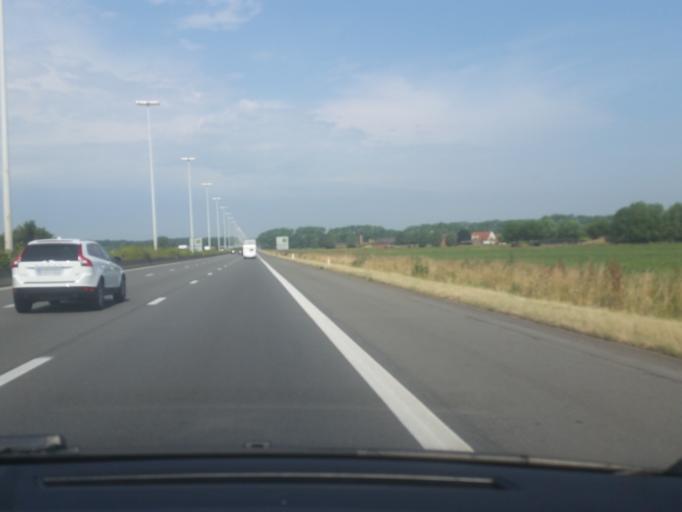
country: BE
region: Flanders
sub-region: Provincie West-Vlaanderen
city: Oostkamp
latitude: 51.1350
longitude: 3.2750
